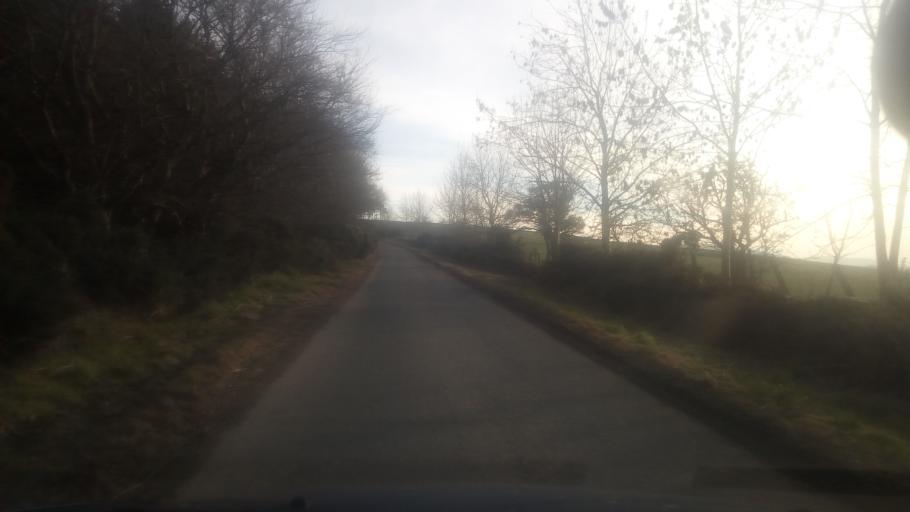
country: GB
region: Scotland
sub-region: The Scottish Borders
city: Jedburgh
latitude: 55.4048
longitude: -2.6007
